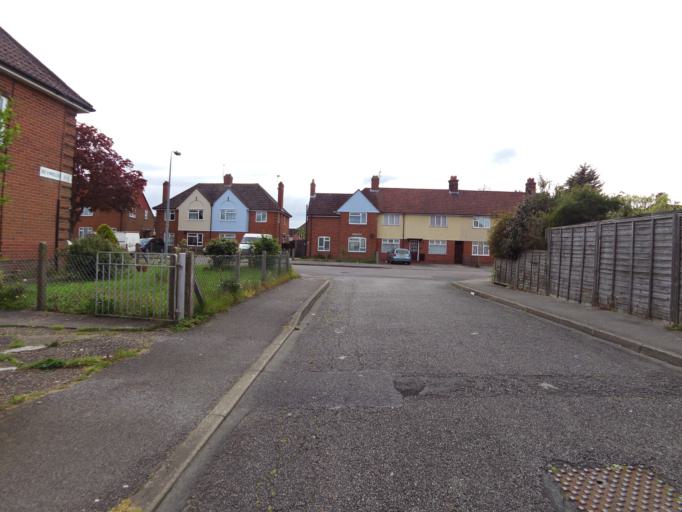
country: GB
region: England
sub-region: Suffolk
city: Ipswich
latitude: 52.0332
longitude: 1.1795
